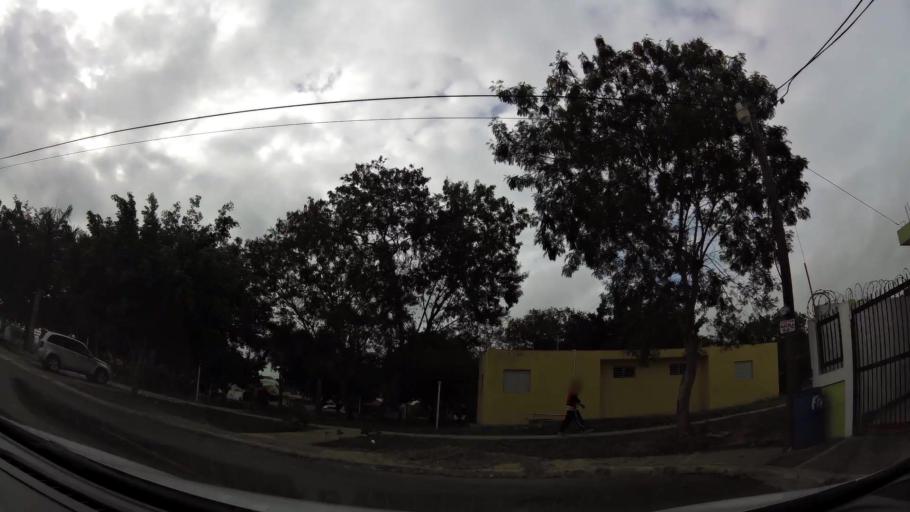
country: DO
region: Santiago
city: Santiago de los Caballeros
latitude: 19.4640
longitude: -70.6591
